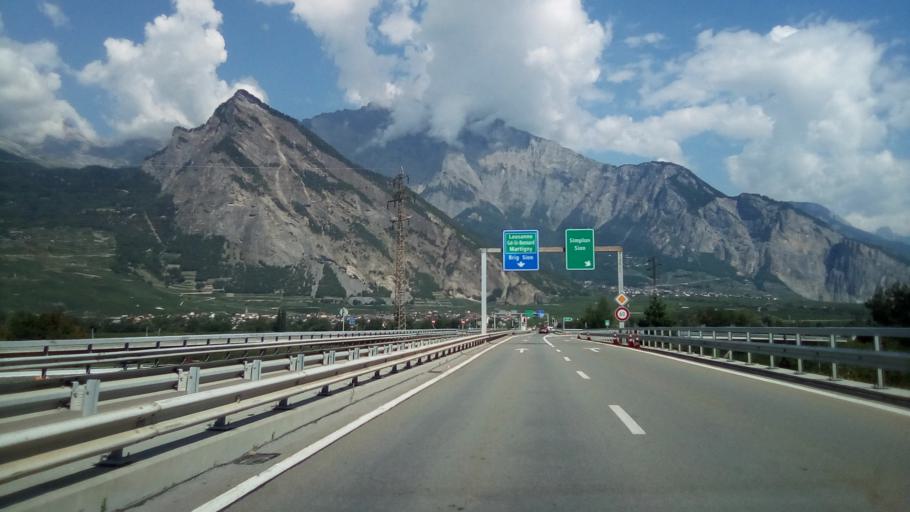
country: CH
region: Valais
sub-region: Martigny District
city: Riddes
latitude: 46.1704
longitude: 7.2144
